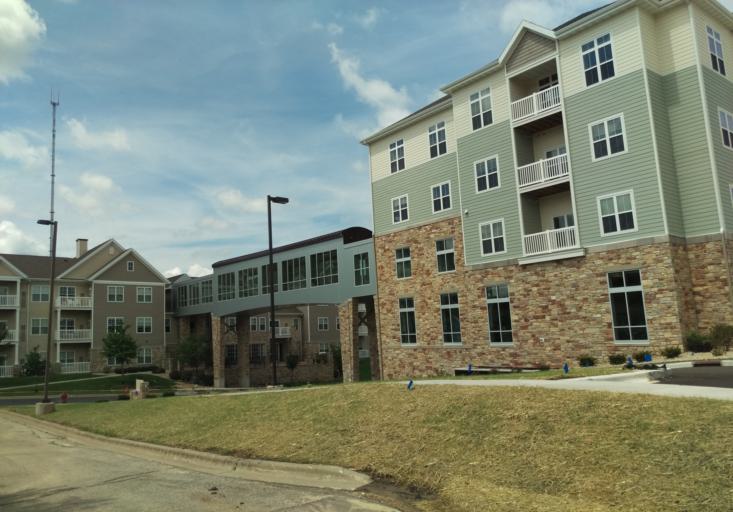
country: US
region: Wisconsin
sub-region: Dane County
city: Middleton
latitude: 43.0540
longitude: -89.5222
